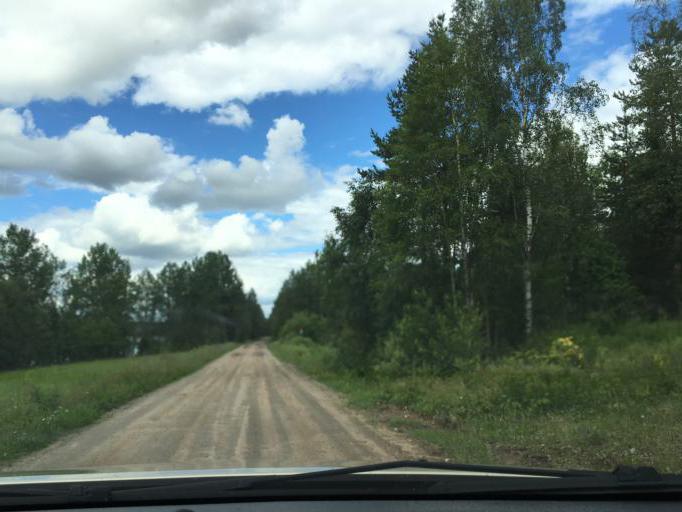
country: SE
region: Norrbotten
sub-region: Overkalix Kommun
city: OEverkalix
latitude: 66.1227
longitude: 22.7859
